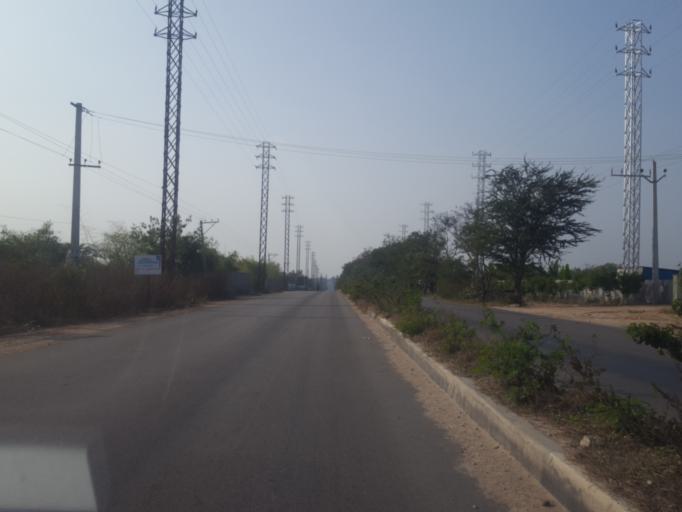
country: IN
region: Telangana
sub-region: Medak
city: Serilingampalle
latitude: 17.4086
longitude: 78.2766
